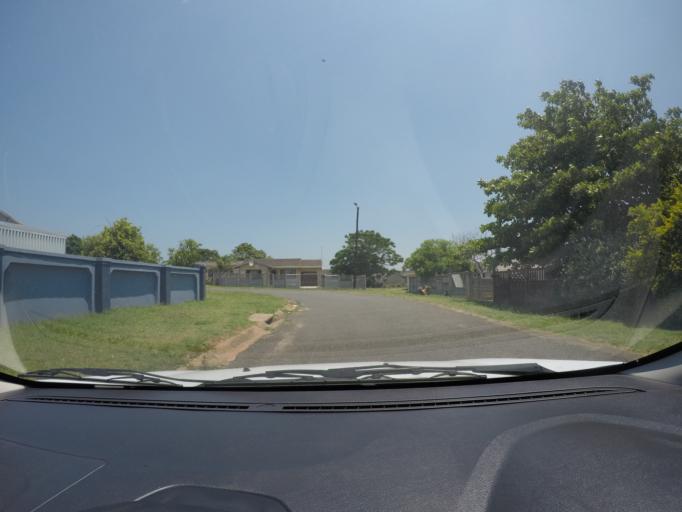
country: ZA
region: KwaZulu-Natal
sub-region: uThungulu District Municipality
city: eSikhawini
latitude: -28.8835
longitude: 31.8889
